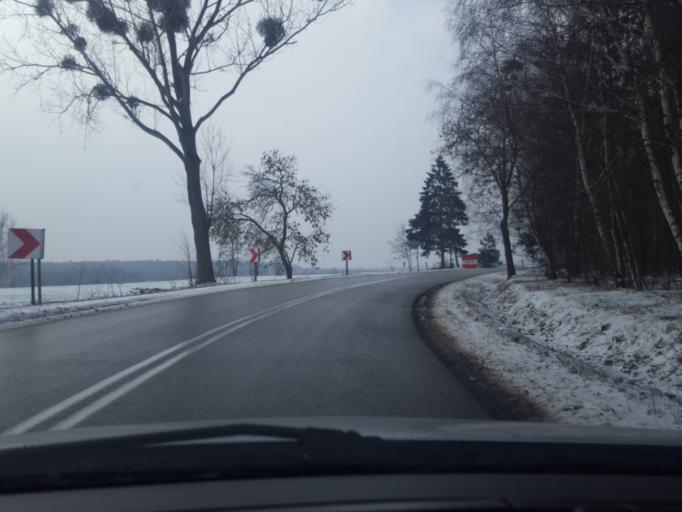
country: PL
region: Lodz Voivodeship
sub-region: Powiat brzezinski
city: Brzeziny
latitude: 51.8333
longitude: 19.8008
